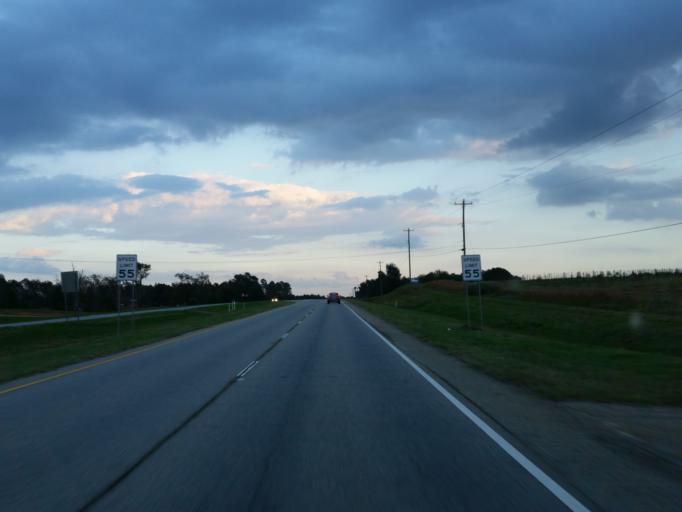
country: US
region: Georgia
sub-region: Pulaski County
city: Hawkinsville
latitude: 32.3109
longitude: -83.5155
